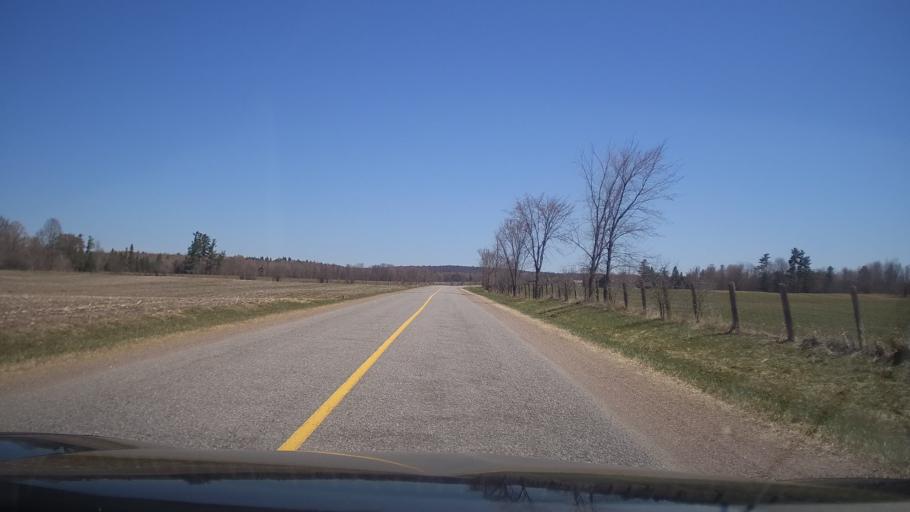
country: CA
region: Quebec
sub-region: Outaouais
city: Shawville
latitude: 45.5427
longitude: -76.3909
